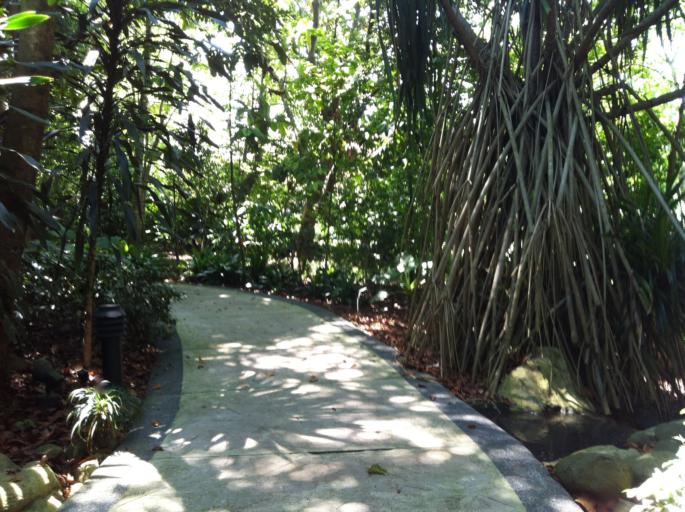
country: SG
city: Singapore
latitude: 1.3078
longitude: 103.8176
